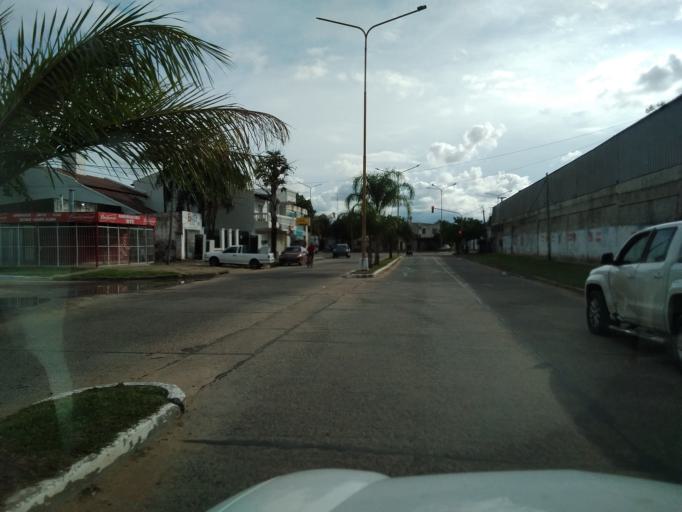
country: AR
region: Corrientes
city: Corrientes
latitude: -27.4614
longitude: -58.7858
